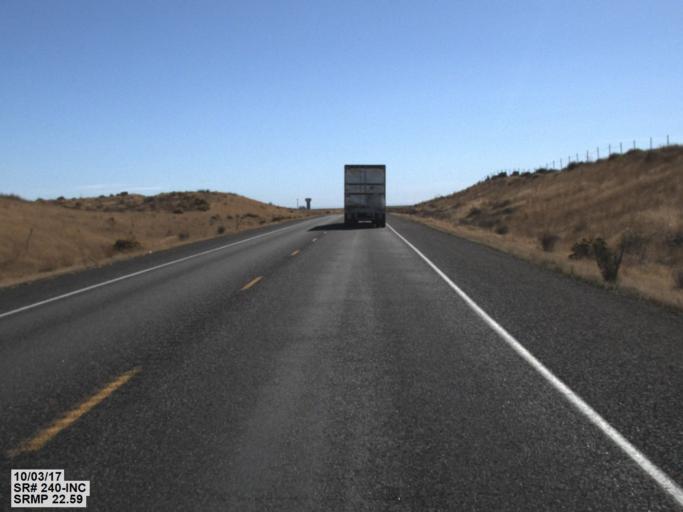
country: US
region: Washington
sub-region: Benton County
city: West Richland
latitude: 46.3643
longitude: -119.3880
